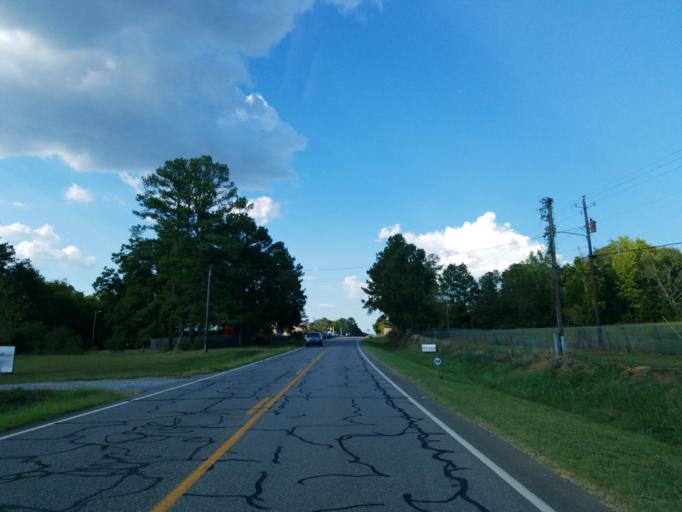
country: US
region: Georgia
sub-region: Bartow County
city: Rydal
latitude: 34.5056
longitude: -84.7101
